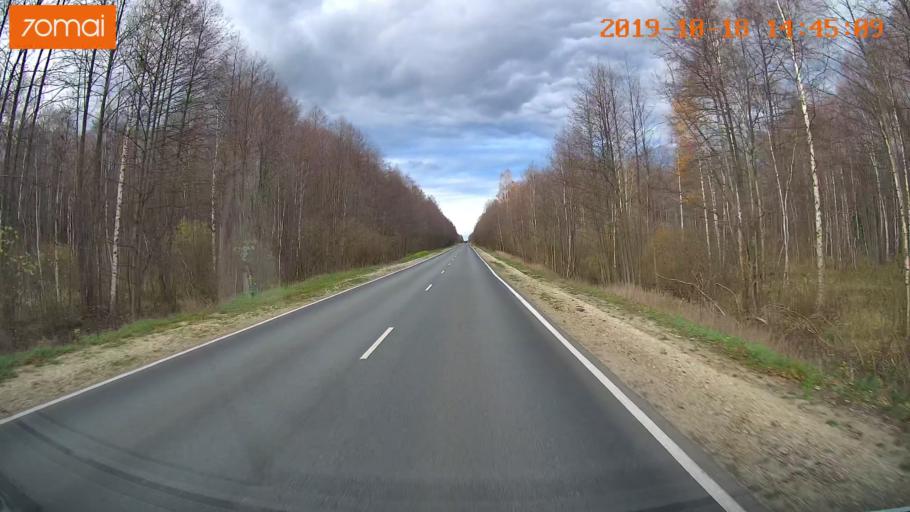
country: RU
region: Vladimir
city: Velikodvorskiy
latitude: 55.3501
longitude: 40.6783
